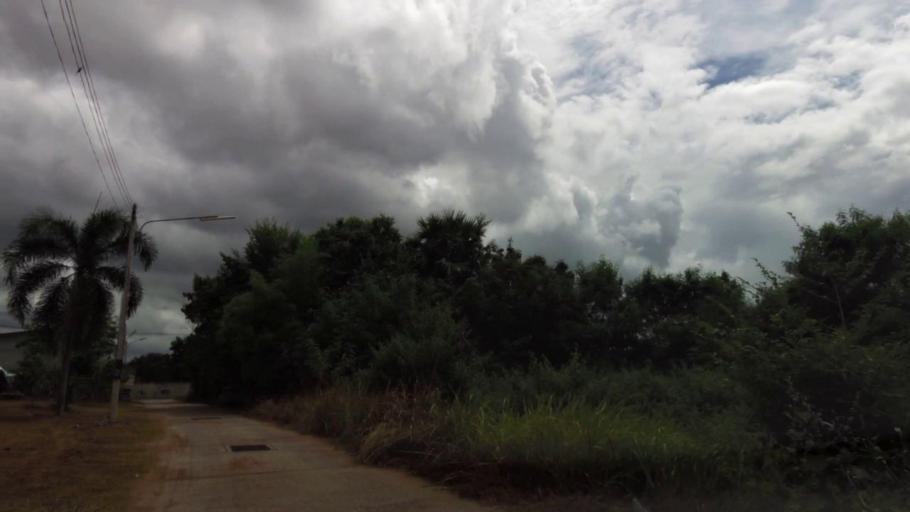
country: TH
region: Nakhon Sawan
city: Phai Sali
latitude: 15.5968
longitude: 100.6486
